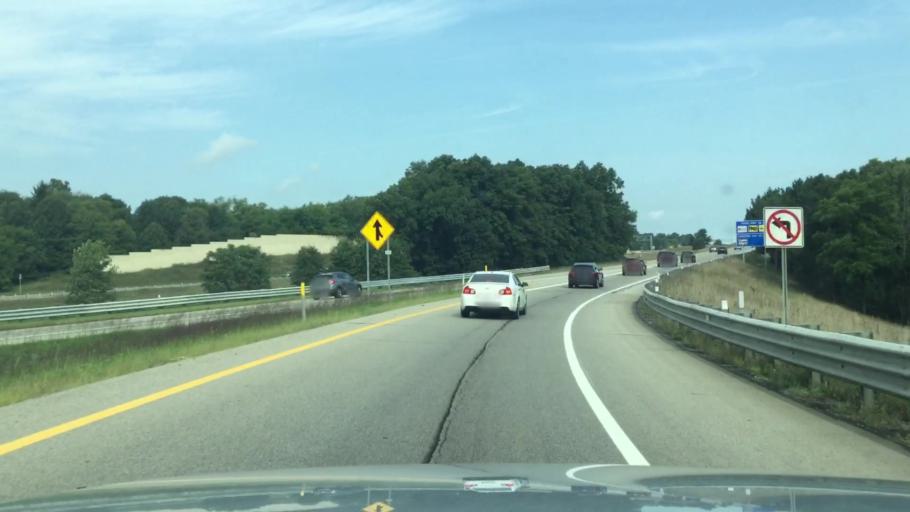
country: US
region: Michigan
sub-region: Kalamazoo County
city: Westwood
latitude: 42.2407
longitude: -85.6375
